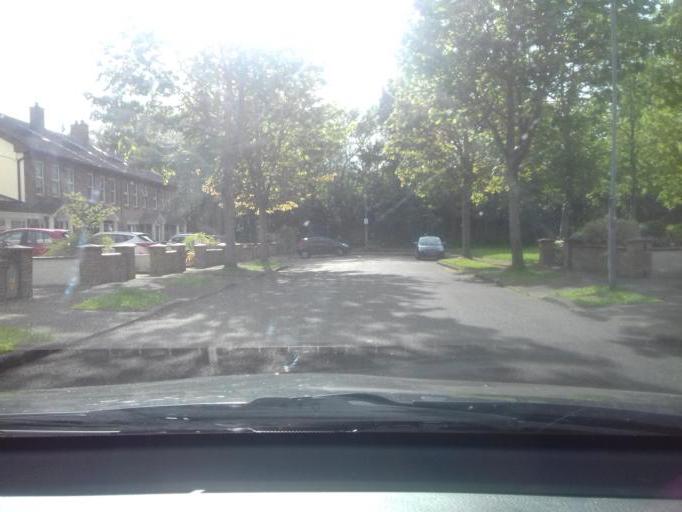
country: IE
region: Leinster
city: Castleknock
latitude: 53.3739
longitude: -6.3709
